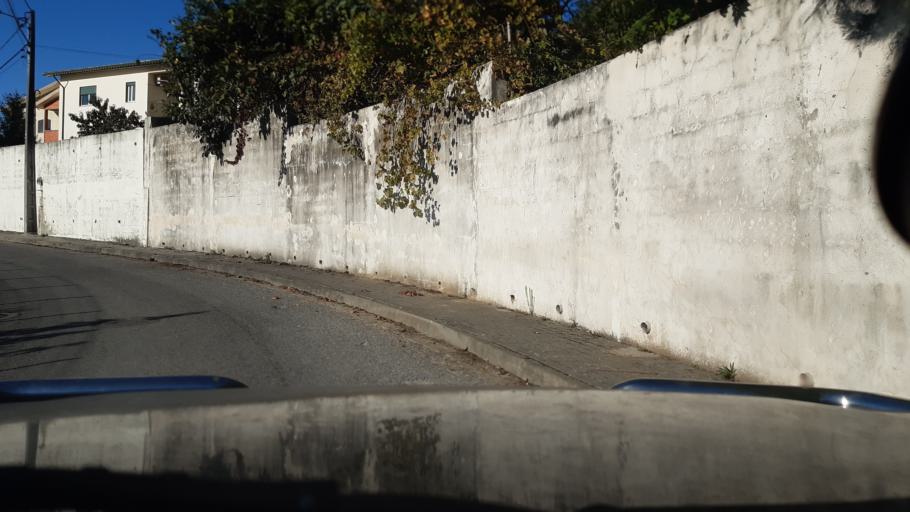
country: PT
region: Aveiro
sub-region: Agueda
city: Agueda
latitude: 40.5555
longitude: -8.4388
